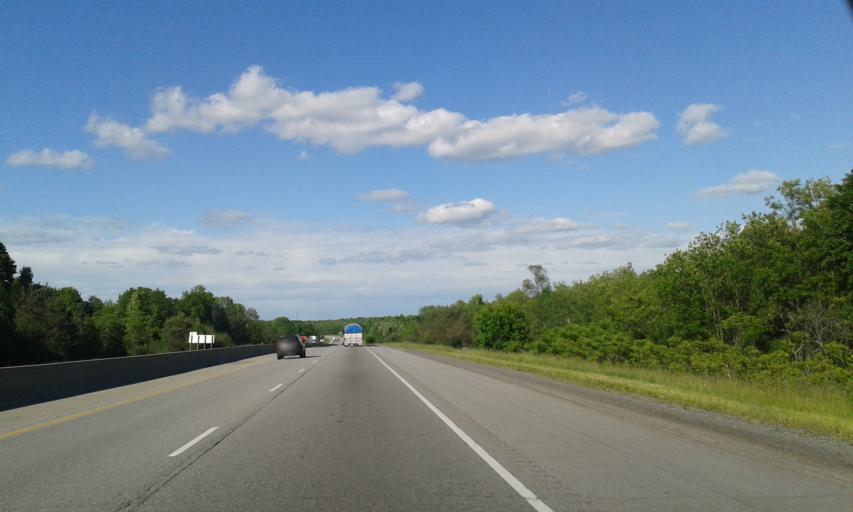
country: CA
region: Ontario
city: Brockville
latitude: 44.6263
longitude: -75.6615
